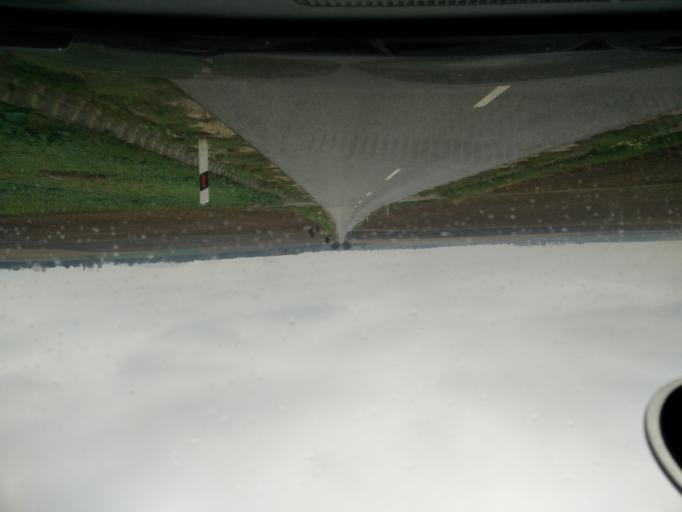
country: HU
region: Komarom-Esztergom
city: Bajna
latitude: 47.6431
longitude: 18.5719
